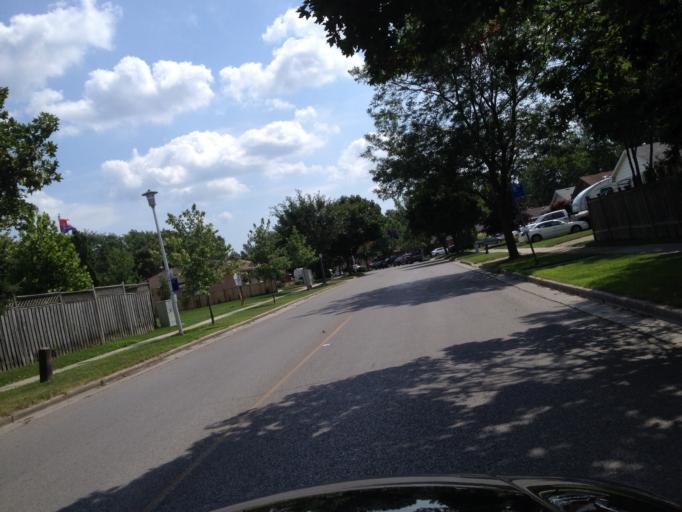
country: CA
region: Ontario
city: London
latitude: 42.9995
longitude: -81.3153
